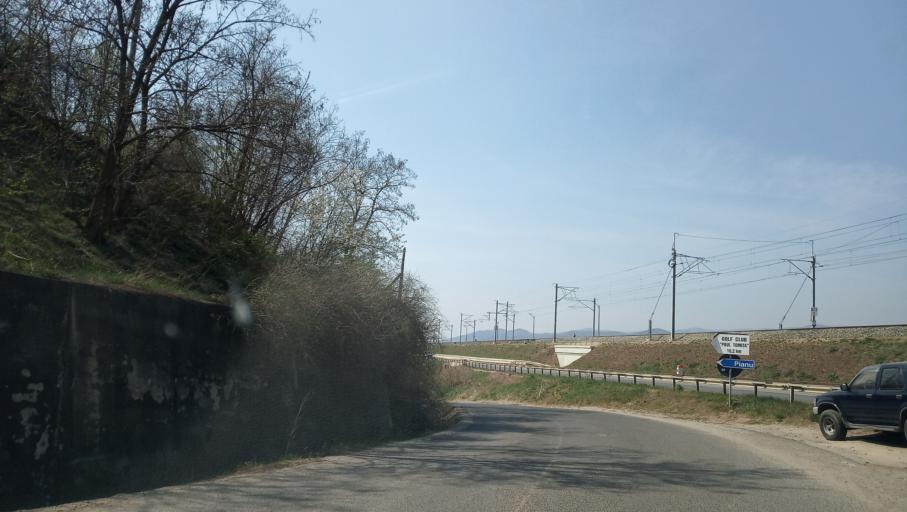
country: RO
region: Alba
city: Vurpar
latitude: 45.9851
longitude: 23.4881
